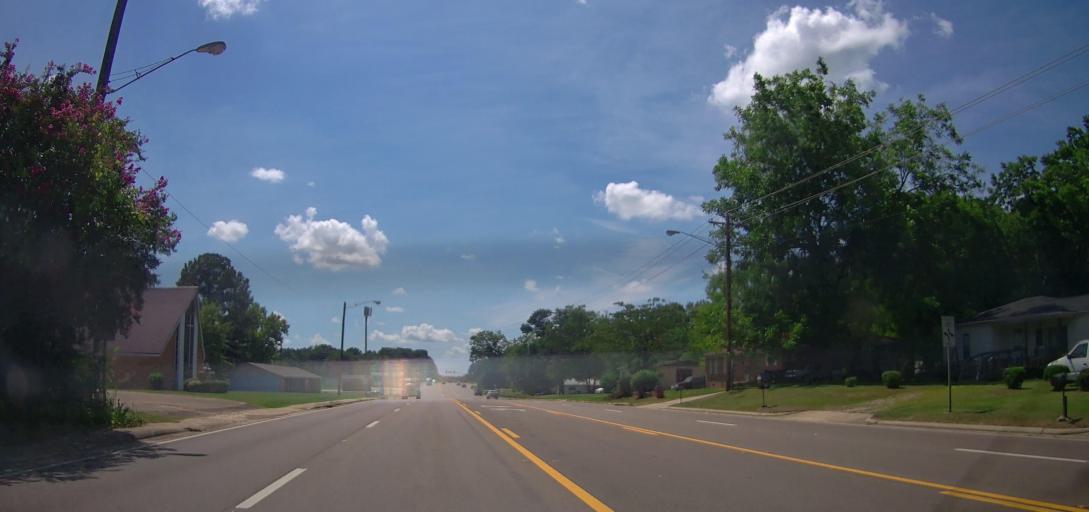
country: US
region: Mississippi
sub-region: Monroe County
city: Aberdeen
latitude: 33.8150
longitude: -88.5490
